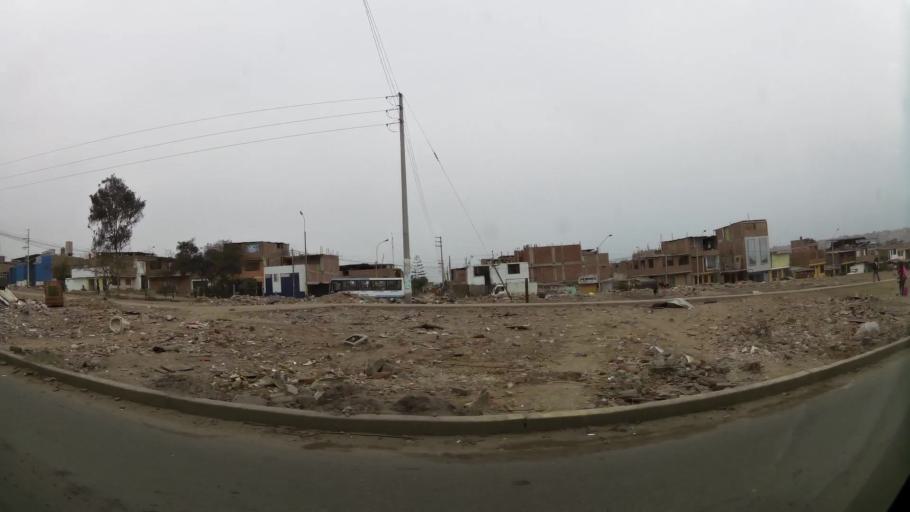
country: PE
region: Lima
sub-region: Lima
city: Surco
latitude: -12.2244
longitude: -76.9385
